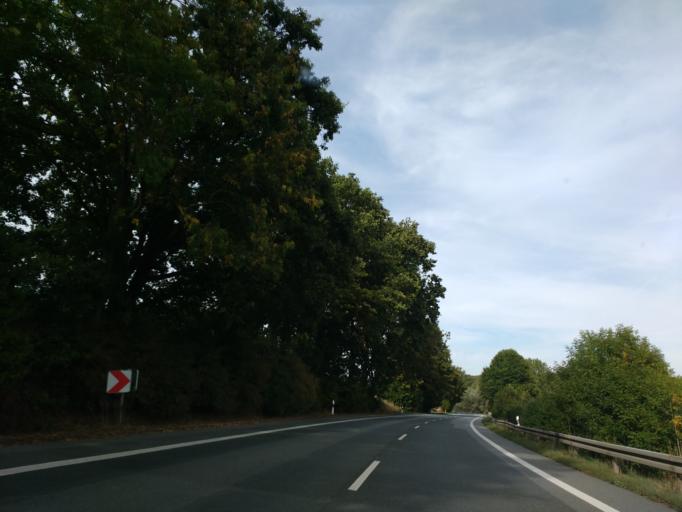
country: DE
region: North Rhine-Westphalia
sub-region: Regierungsbezirk Detmold
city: Willebadessen
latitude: 51.6318
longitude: 9.1346
